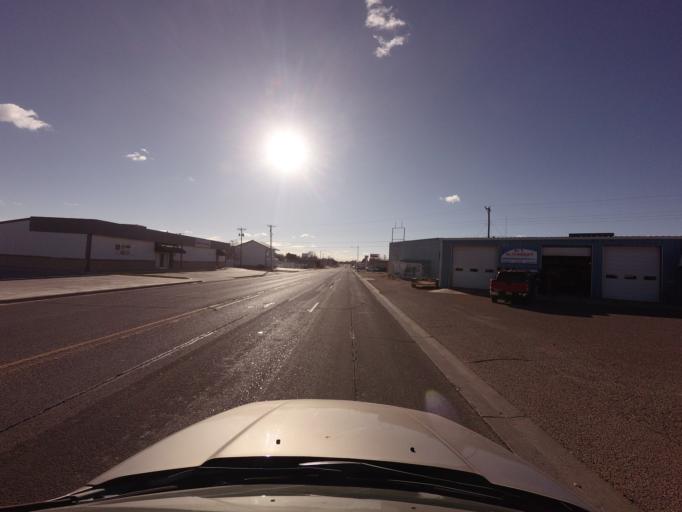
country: US
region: New Mexico
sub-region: Curry County
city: Clovis
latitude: 34.4175
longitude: -103.1980
